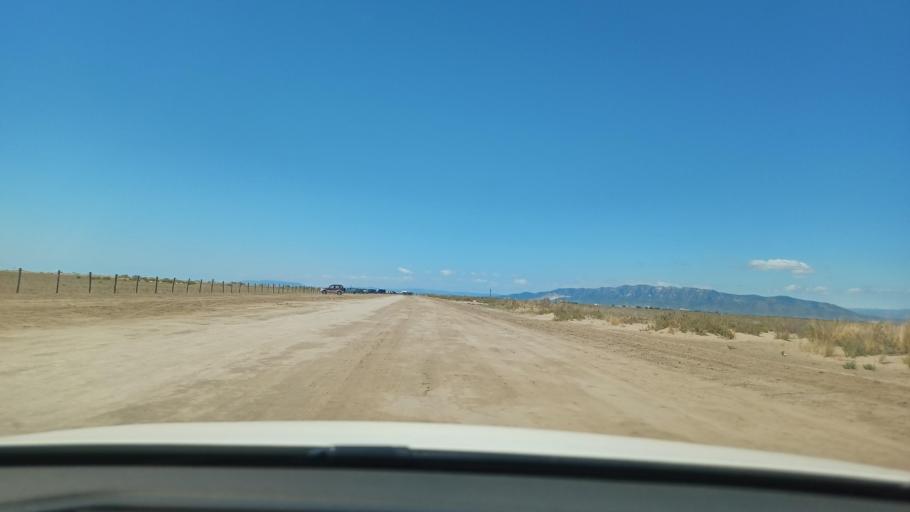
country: ES
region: Catalonia
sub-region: Provincia de Tarragona
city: Deltebre
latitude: 40.6518
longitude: 0.7784
